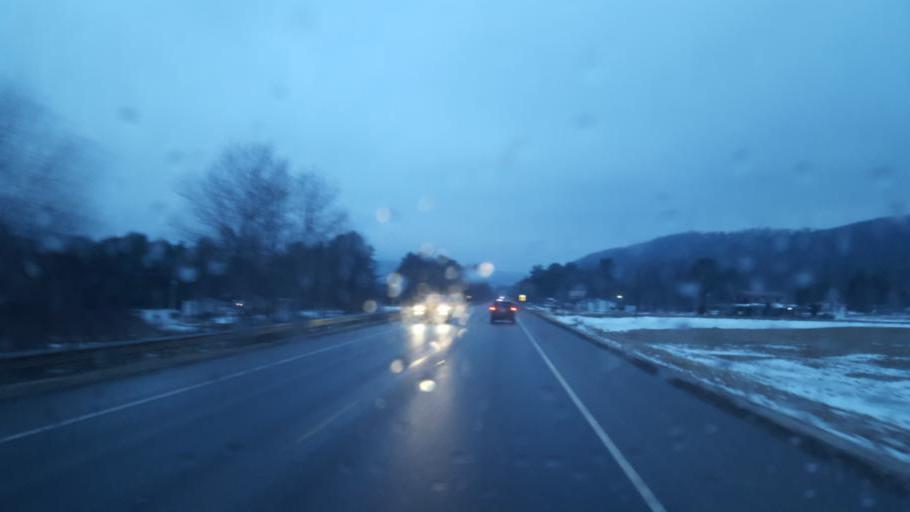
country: US
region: Pennsylvania
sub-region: McKean County
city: Port Allegany
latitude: 41.7947
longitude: -78.2500
